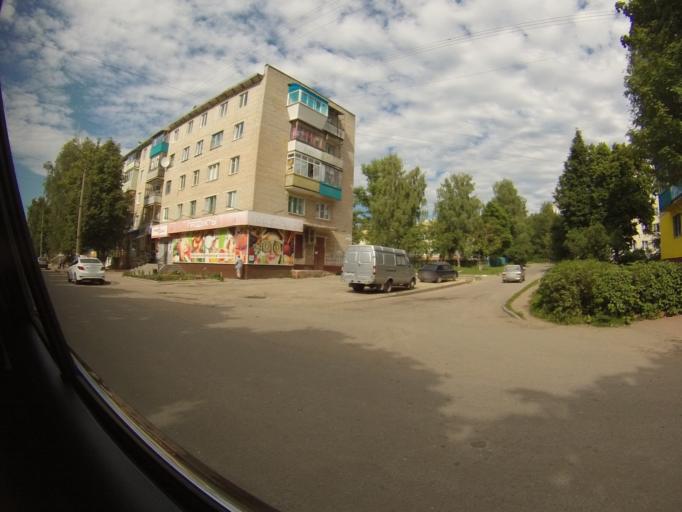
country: RU
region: Orjol
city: Mtsensk
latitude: 53.2923
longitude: 36.5945
